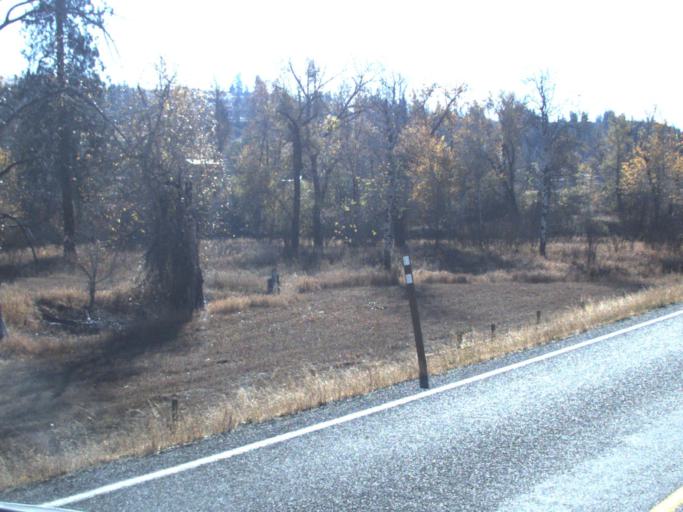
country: CA
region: British Columbia
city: Grand Forks
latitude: 48.8827
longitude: -118.6035
